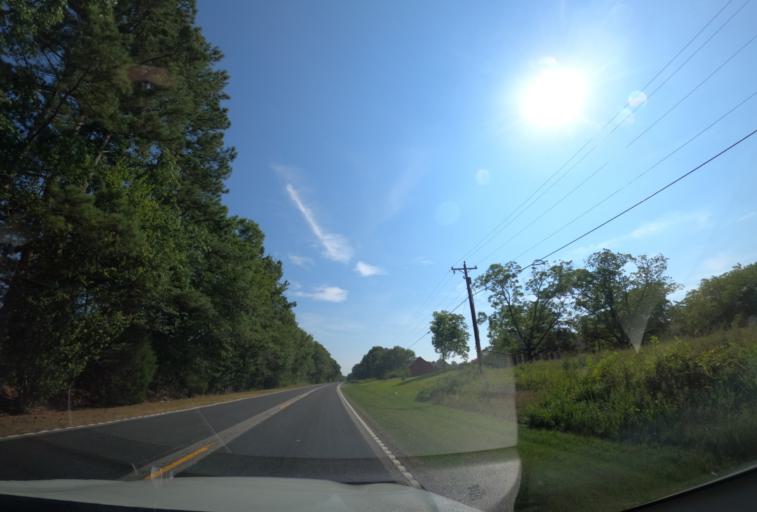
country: US
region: South Carolina
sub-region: Anderson County
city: Belton
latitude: 34.4614
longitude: -82.5402
